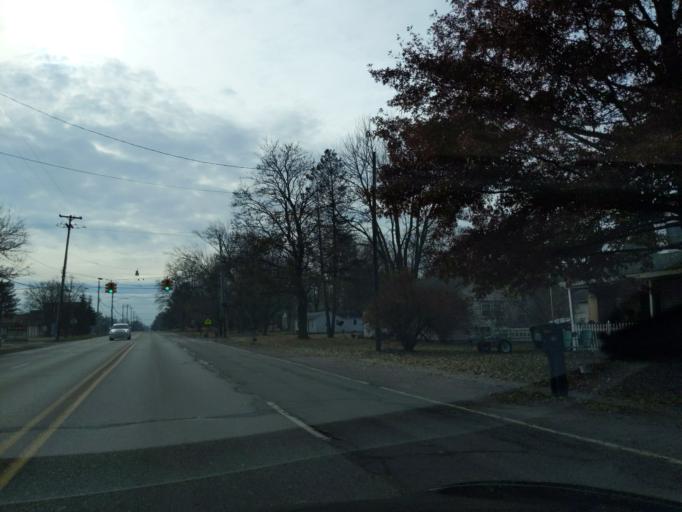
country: US
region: Michigan
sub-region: Ingham County
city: Holt
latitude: 42.6369
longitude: -84.5234
